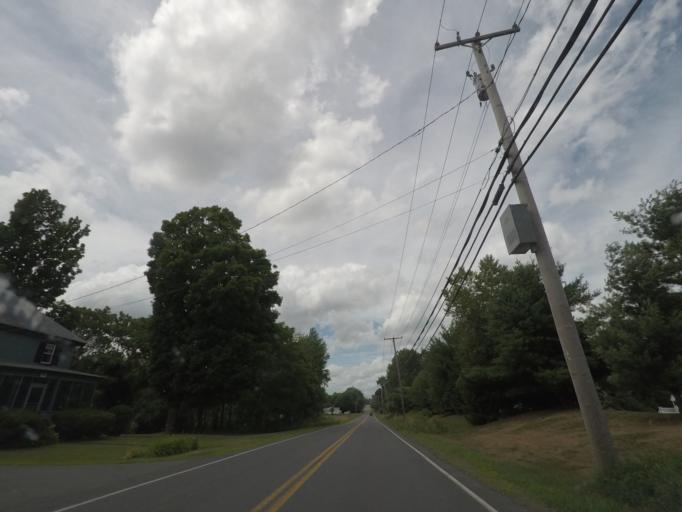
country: US
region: New York
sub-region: Rensselaer County
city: Wynantskill
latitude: 42.7068
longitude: -73.6223
